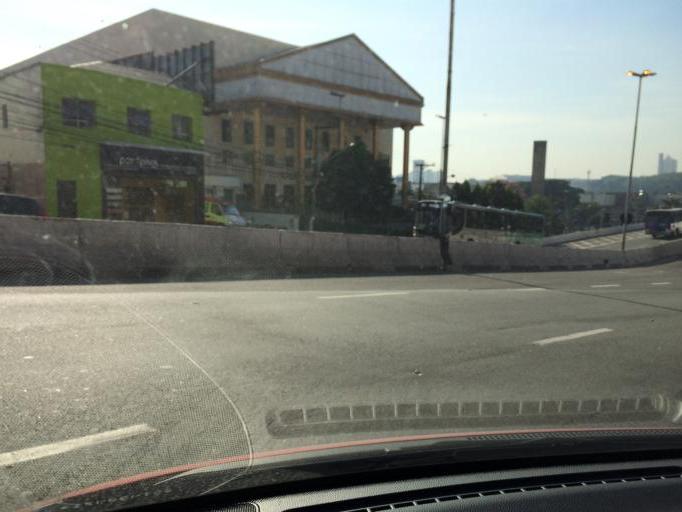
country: BR
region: Sao Paulo
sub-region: Osasco
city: Osasco
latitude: -23.5385
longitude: -46.7748
